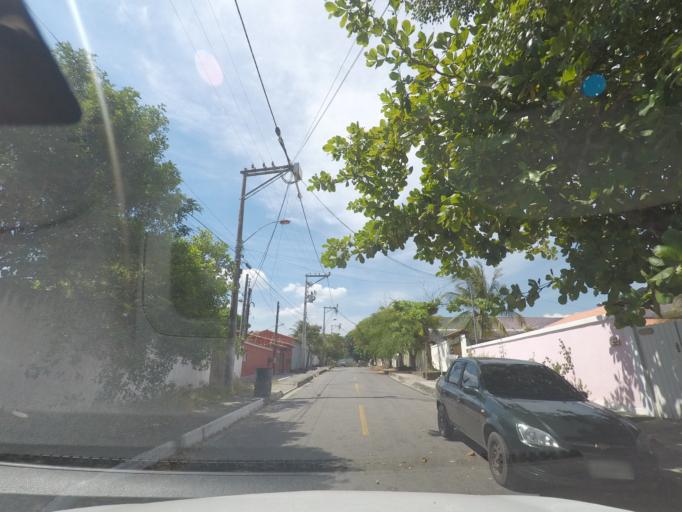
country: BR
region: Rio de Janeiro
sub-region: Marica
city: Marica
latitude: -22.9664
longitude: -42.9640
